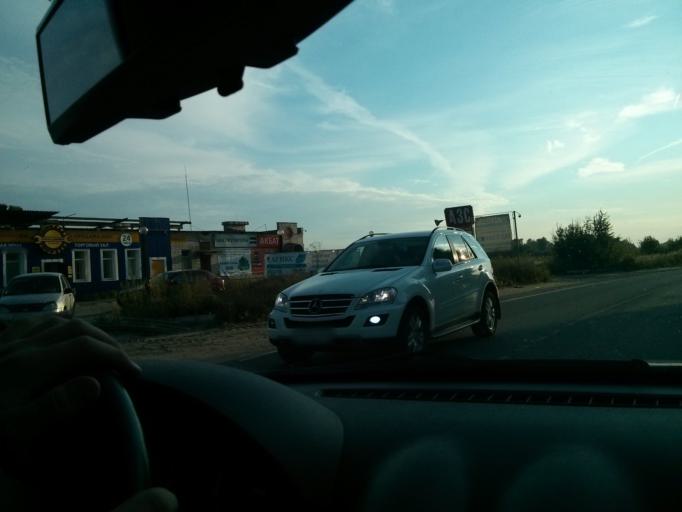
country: RU
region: Vladimir
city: Murom
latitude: 55.5614
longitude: 42.0407
